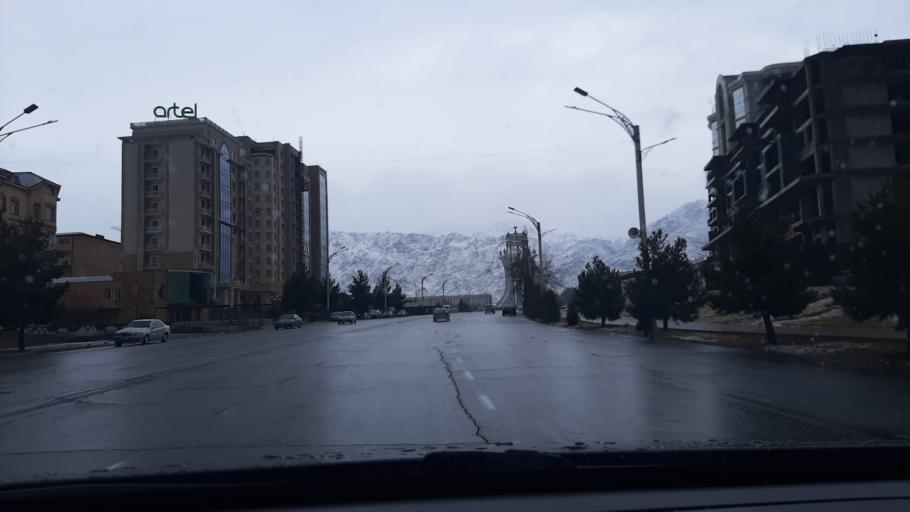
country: TJ
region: Viloyati Sughd
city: Khujand
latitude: 40.2983
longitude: 69.6153
